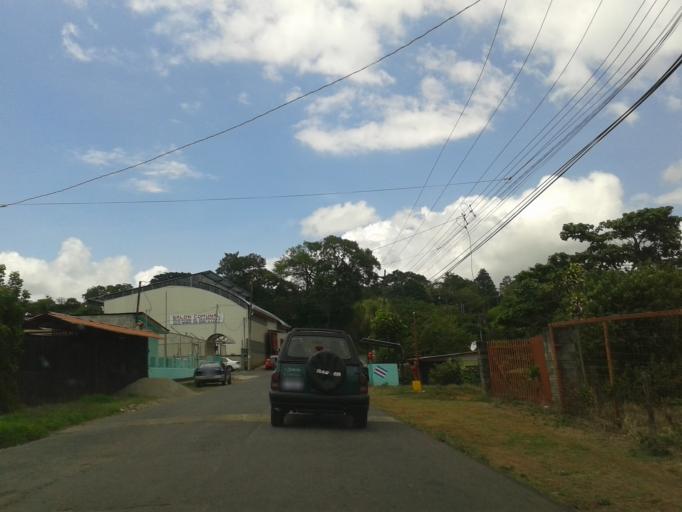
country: CR
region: Alajuela
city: Sabanilla
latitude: 10.1096
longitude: -84.1911
